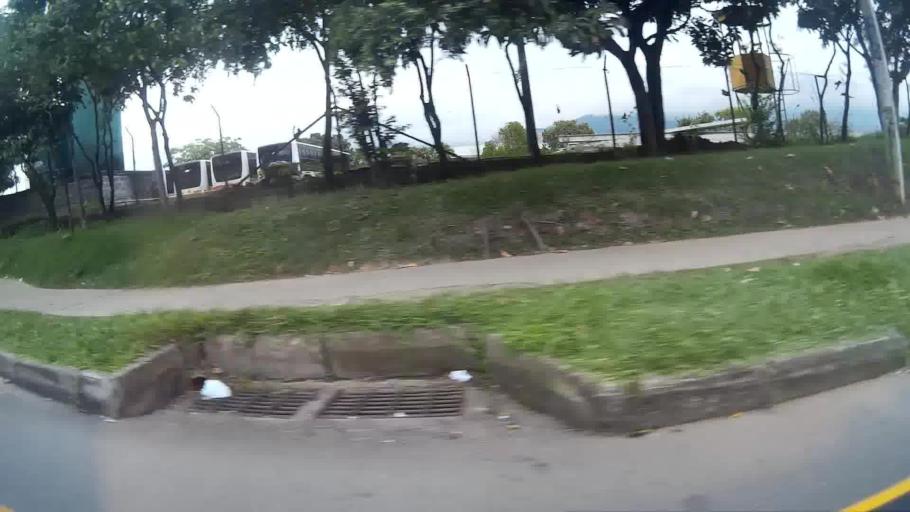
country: CO
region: Antioquia
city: Medellin
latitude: 6.2303
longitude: -75.5872
